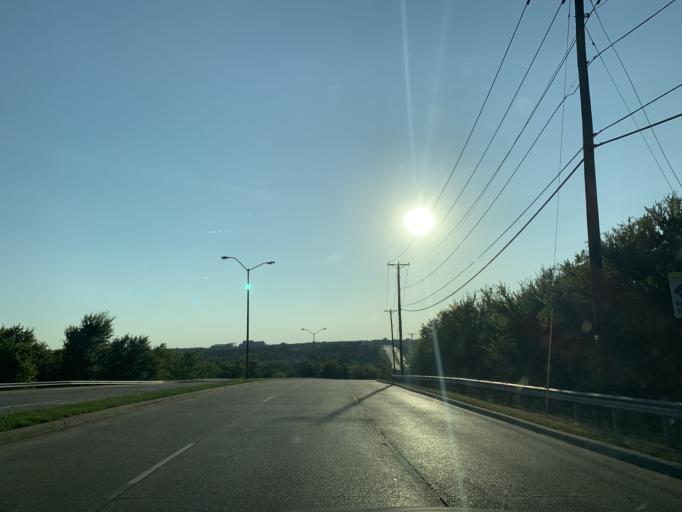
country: US
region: Texas
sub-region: Dallas County
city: Hutchins
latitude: 32.6626
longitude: -96.7844
